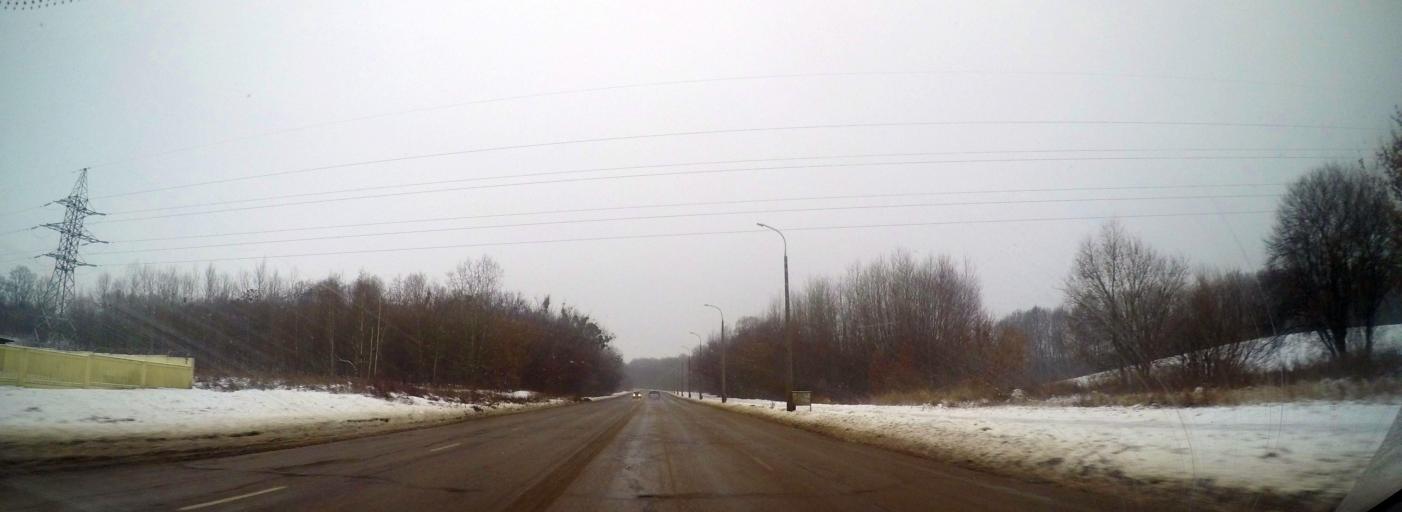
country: BY
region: Grodnenskaya
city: Hrodna
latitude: 53.6829
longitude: 23.8814
